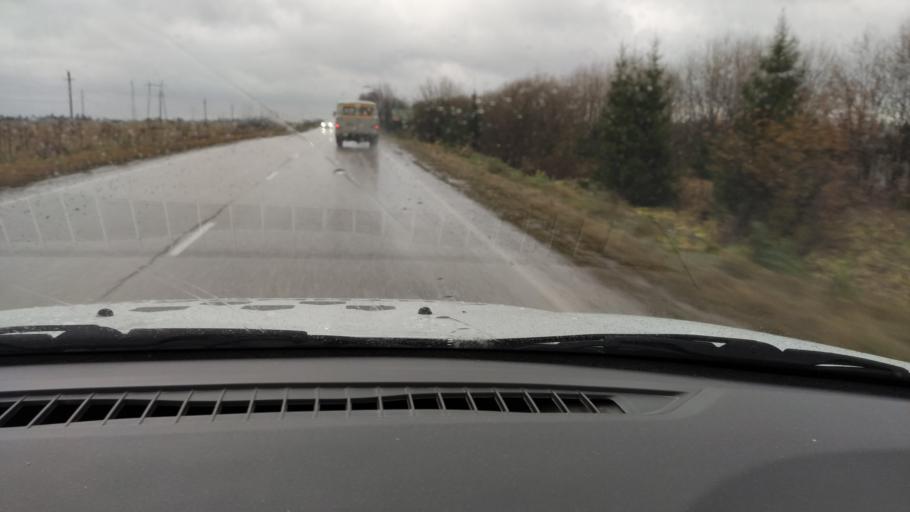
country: RU
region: Perm
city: Sylva
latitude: 58.0292
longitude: 56.7016
